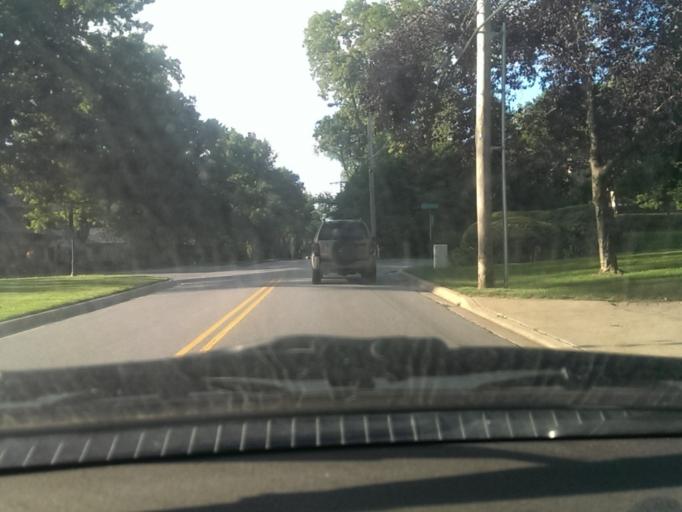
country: US
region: Kansas
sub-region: Johnson County
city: Mission Hills
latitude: 39.0189
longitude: -94.6077
